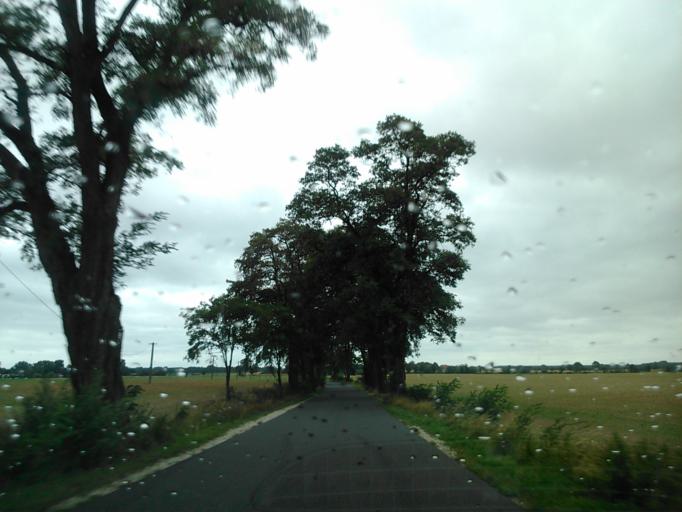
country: PL
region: Kujawsko-Pomorskie
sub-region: Powiat radziejowski
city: Piotrkow Kujawski
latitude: 52.5911
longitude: 18.4044
